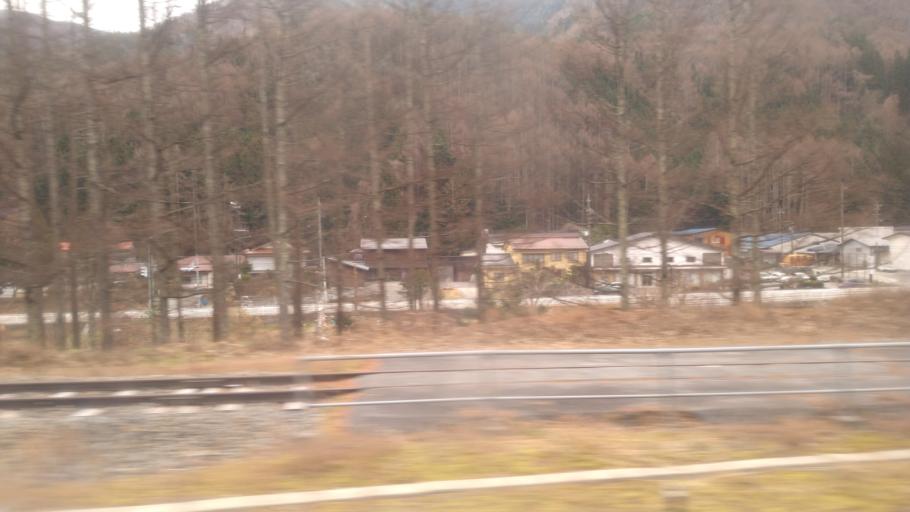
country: JP
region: Nagano
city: Tatsuno
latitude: 35.9714
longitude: 137.8178
